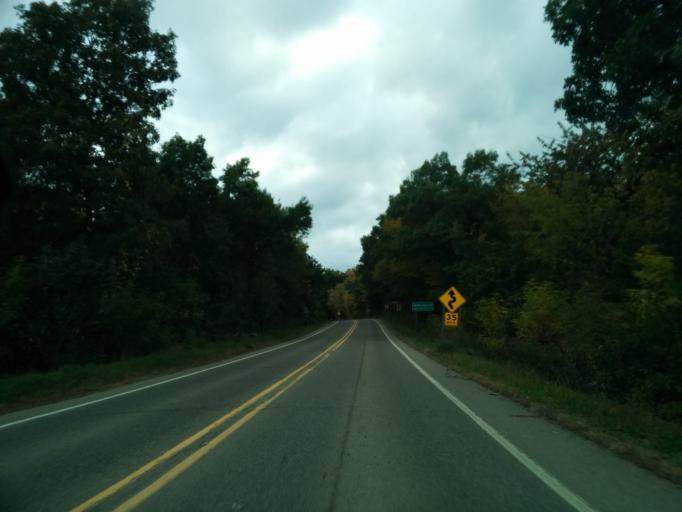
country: US
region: Michigan
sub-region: Oakland County
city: Holly
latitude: 42.8158
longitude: -83.5558
